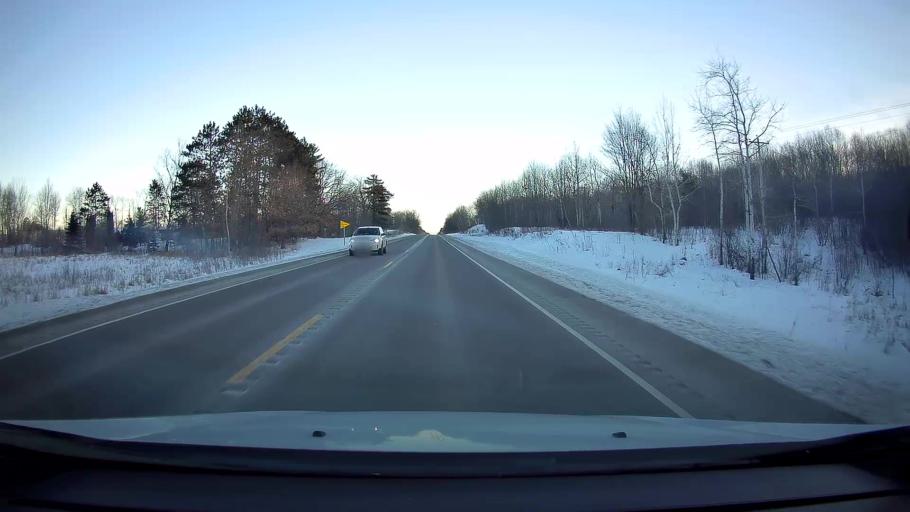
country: US
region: Wisconsin
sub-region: Washburn County
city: Shell Lake
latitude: 45.6849
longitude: -91.9789
